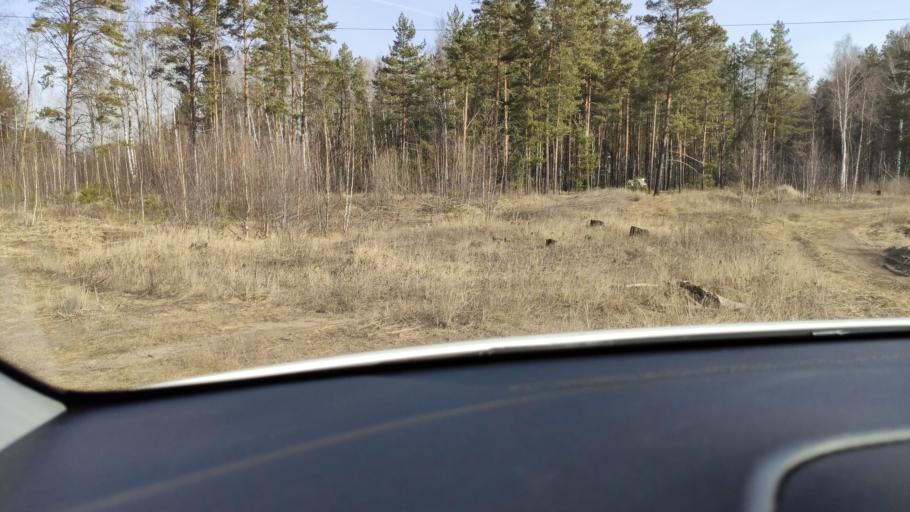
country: RU
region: Tatarstan
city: Vysokaya Gora
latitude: 55.8992
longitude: 49.2068
